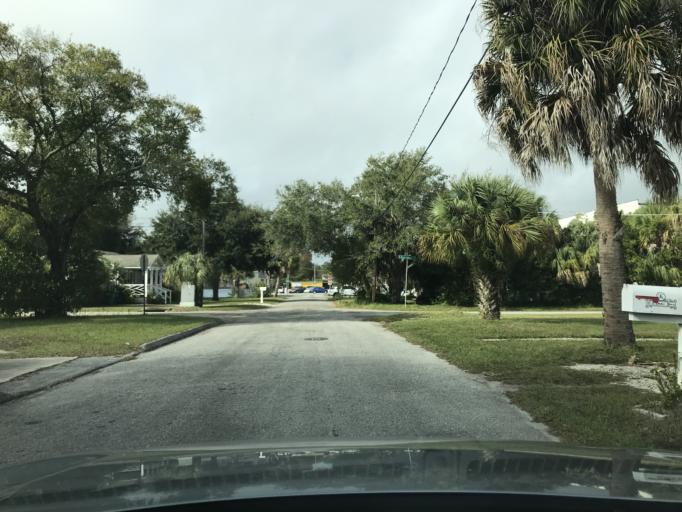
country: US
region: Florida
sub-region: Hillsborough County
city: Tampa
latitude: 27.9860
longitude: -82.4580
